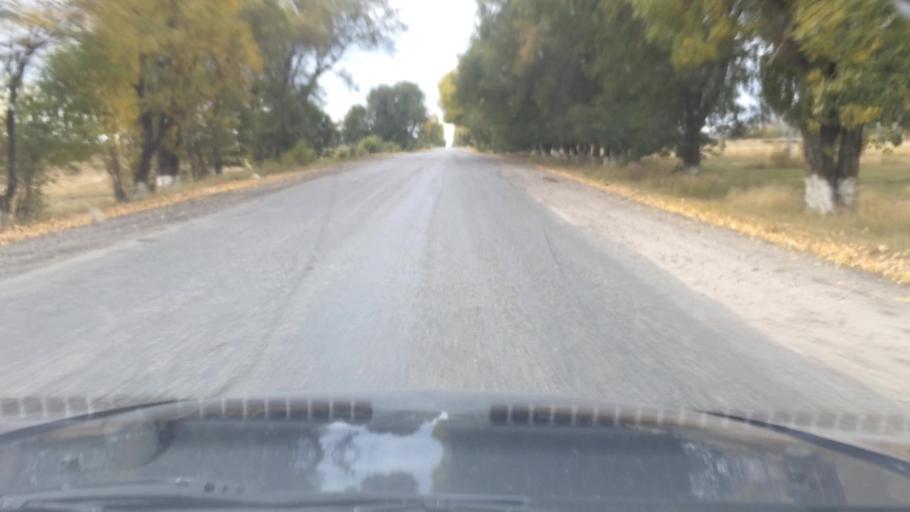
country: KG
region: Ysyk-Koel
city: Tyup
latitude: 42.7752
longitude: 78.2020
